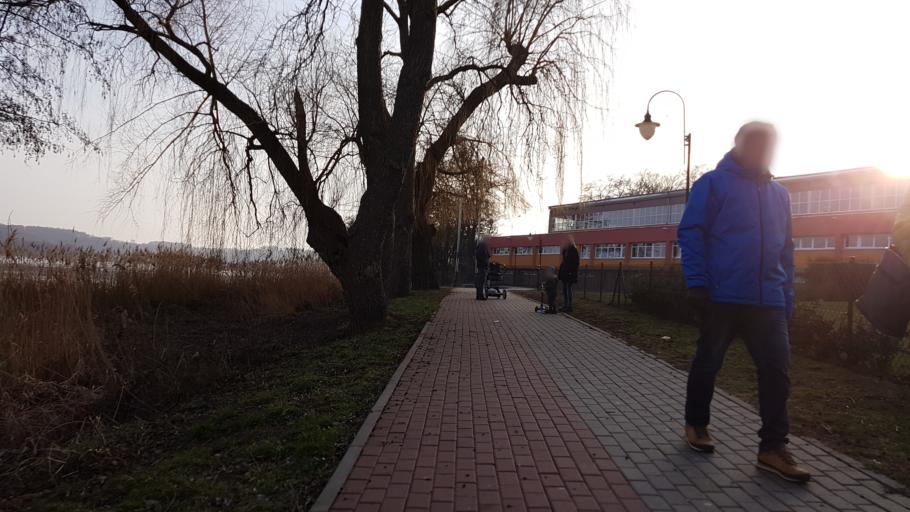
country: PL
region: West Pomeranian Voivodeship
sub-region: Powiat mysliborski
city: Barlinek
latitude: 52.9897
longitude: 15.2181
